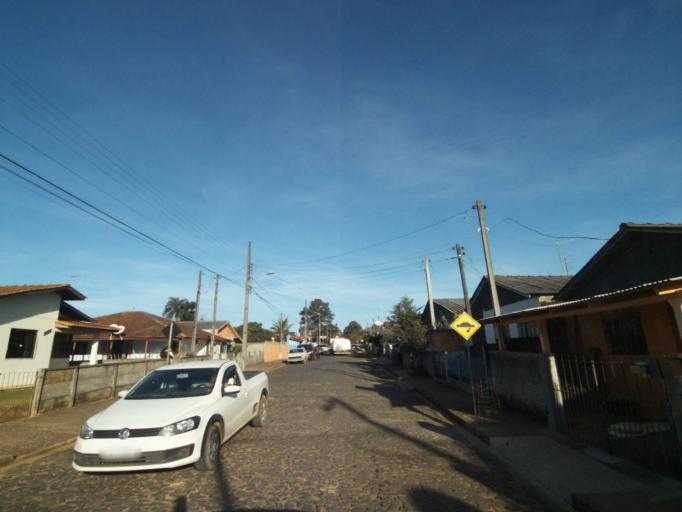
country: BR
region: Parana
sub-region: Tibagi
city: Tibagi
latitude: -24.5087
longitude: -50.4144
